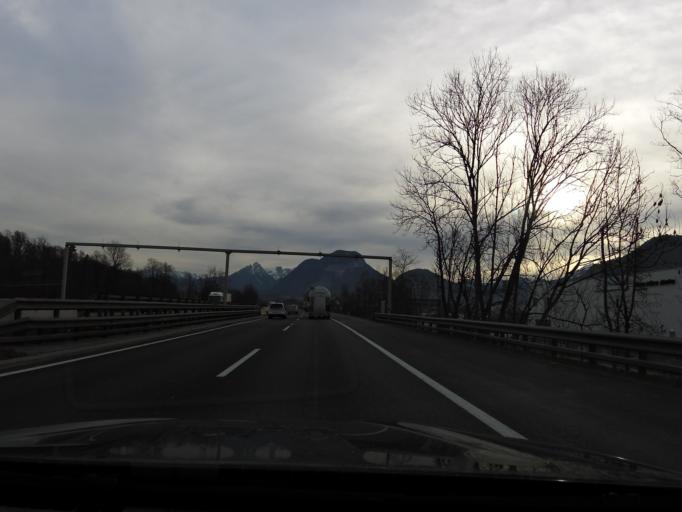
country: AT
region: Tyrol
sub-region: Politischer Bezirk Kufstein
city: Worgl
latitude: 47.4857
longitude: 12.0405
